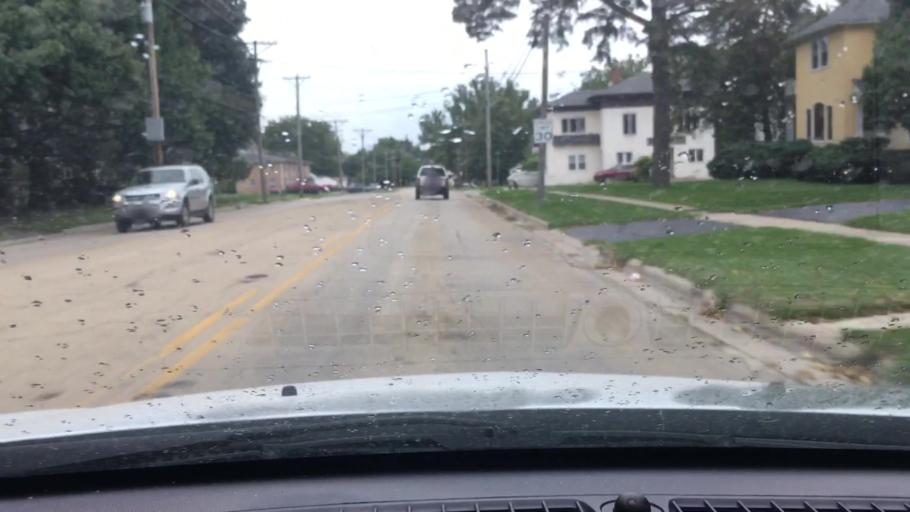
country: US
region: Illinois
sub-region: Ogle County
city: Rochelle
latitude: 41.9159
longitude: -89.0615
